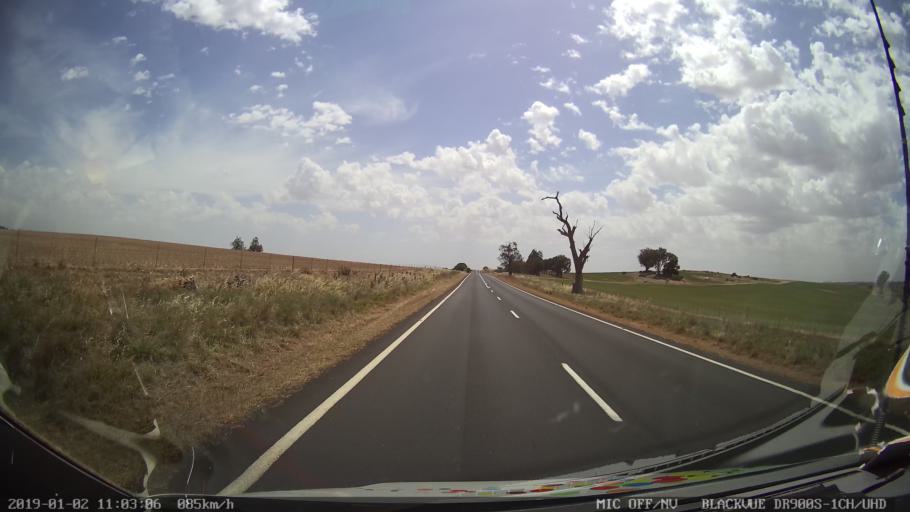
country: AU
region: New South Wales
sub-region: Young
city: Young
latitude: -34.5802
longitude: 148.3340
